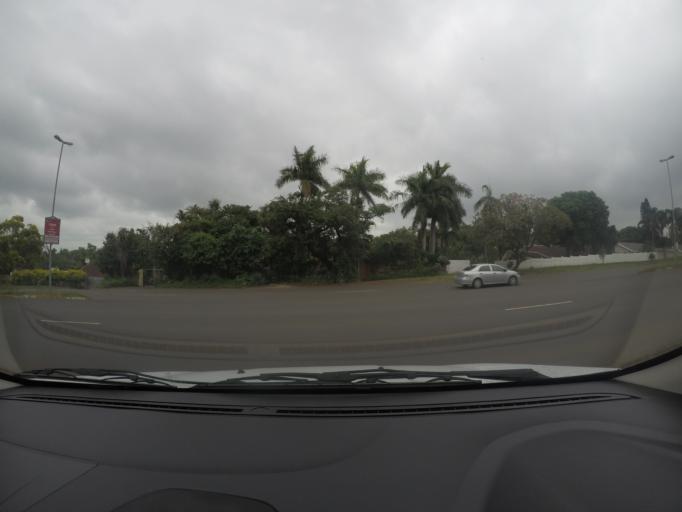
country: ZA
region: KwaZulu-Natal
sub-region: uThungulu District Municipality
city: Empangeni
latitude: -28.7663
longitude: 31.8955
